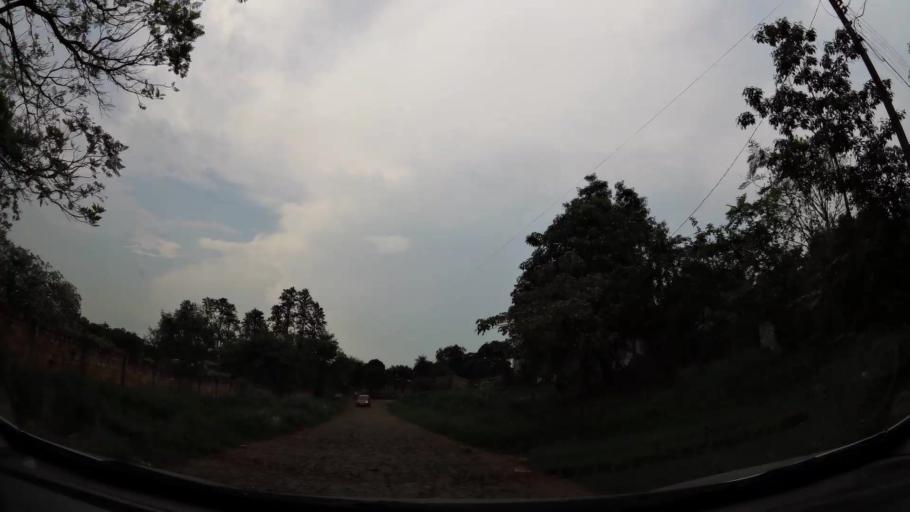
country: PY
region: Alto Parana
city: Presidente Franco
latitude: -25.5450
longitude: -54.6056
